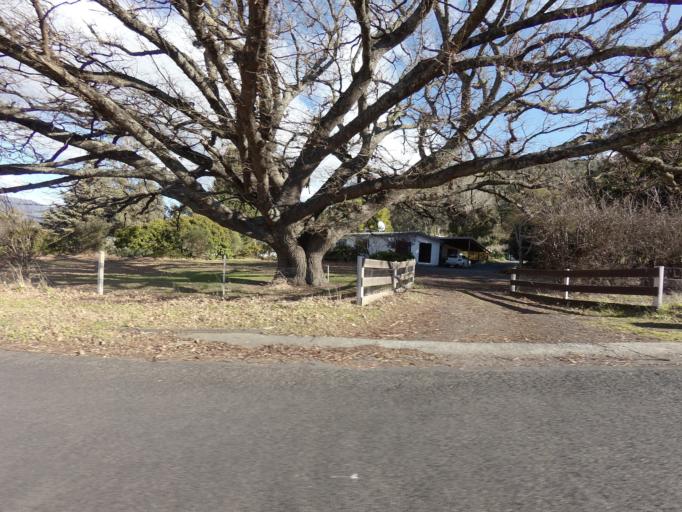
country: AU
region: Tasmania
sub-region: Derwent Valley
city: New Norfolk
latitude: -42.7489
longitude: 147.0459
